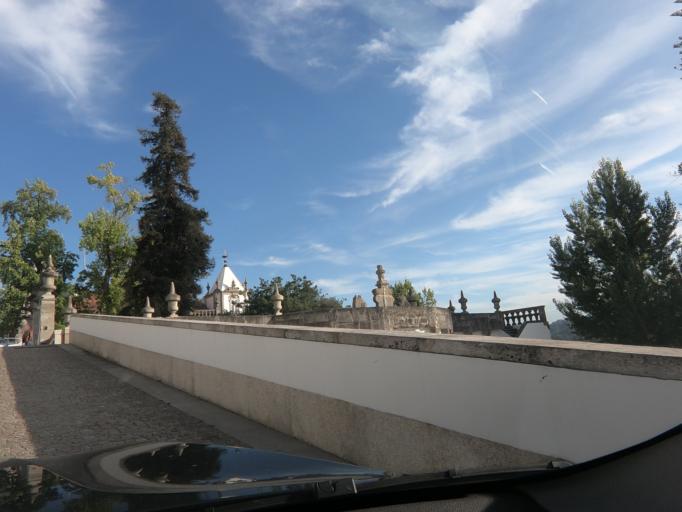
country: PT
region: Porto
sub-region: Gondomar
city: Valbom
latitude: 41.1430
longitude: -8.5756
